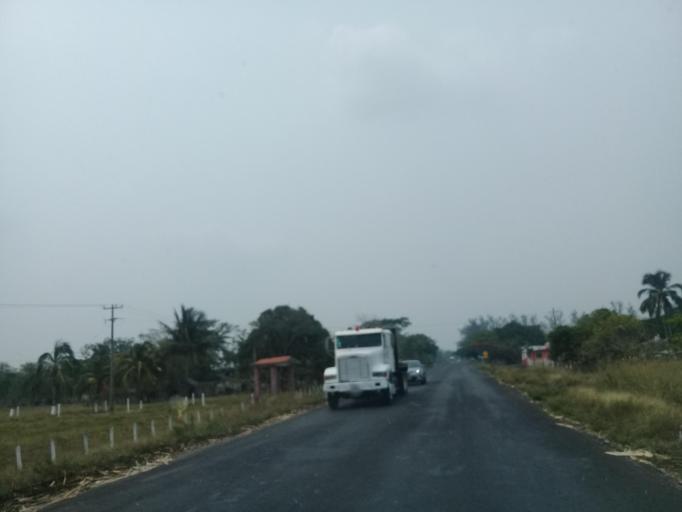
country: MX
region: Veracruz
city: Jamapa
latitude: 18.9469
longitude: -96.1977
